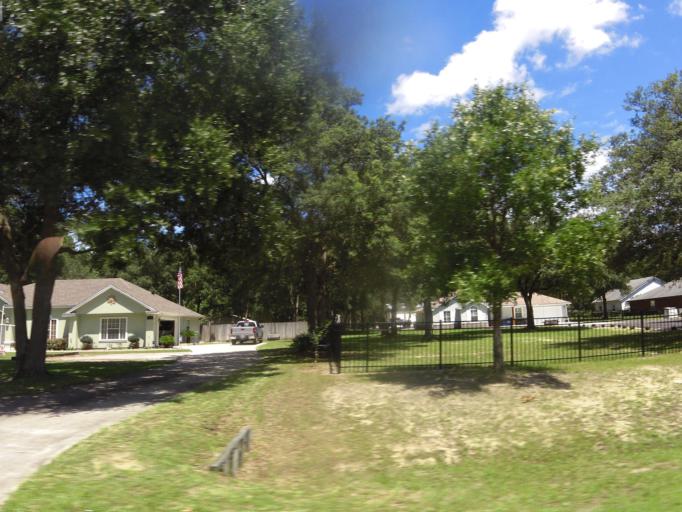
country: US
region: Florida
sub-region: Nassau County
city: Yulee
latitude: 30.6560
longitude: -81.5427
